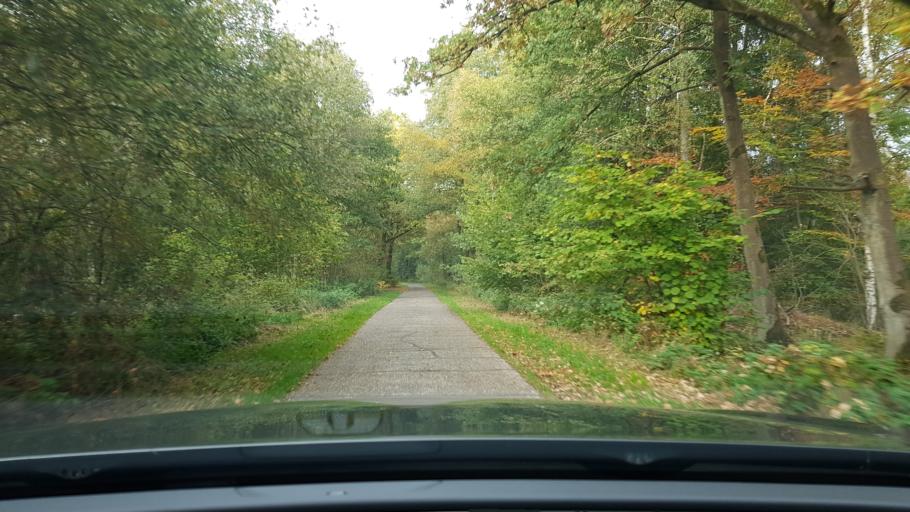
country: DE
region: Lower Saxony
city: Beverstedt
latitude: 53.4177
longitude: 8.8110
